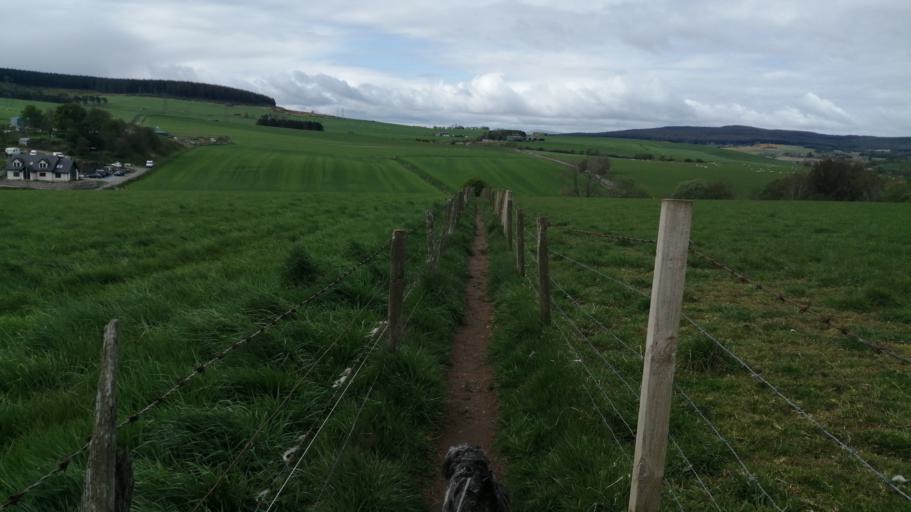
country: GB
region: Scotland
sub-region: Moray
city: Keith
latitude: 57.5317
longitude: -2.9598
